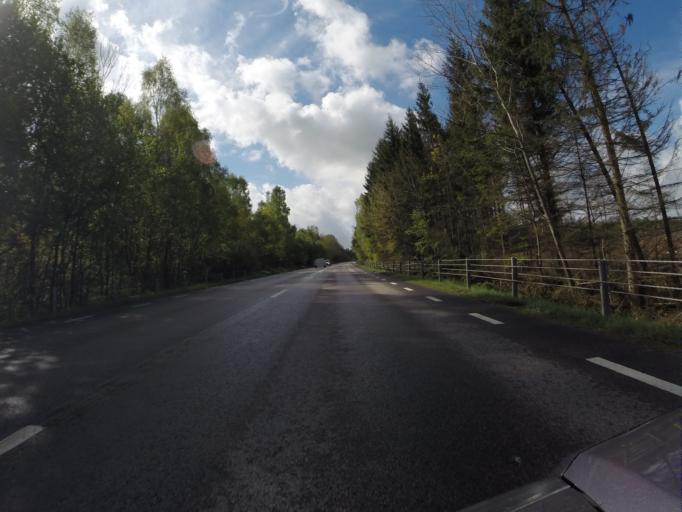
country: SE
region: Skane
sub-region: Bjuvs Kommun
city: Billesholm
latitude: 56.0382
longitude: 12.9698
